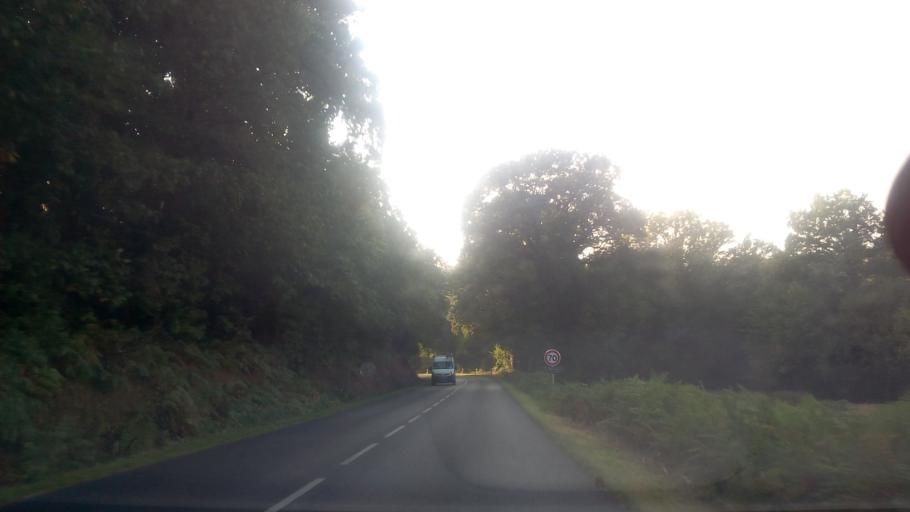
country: FR
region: Brittany
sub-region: Departement du Morbihan
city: Saint-Jean-la-Poterie
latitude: 47.6254
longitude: -2.1243
